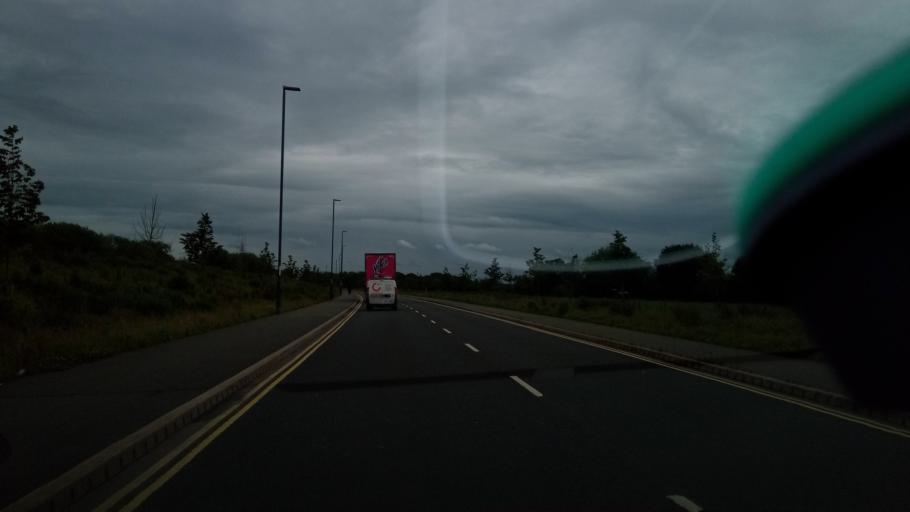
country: GB
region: England
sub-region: Derby
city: Derby
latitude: 52.8710
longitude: -1.4572
